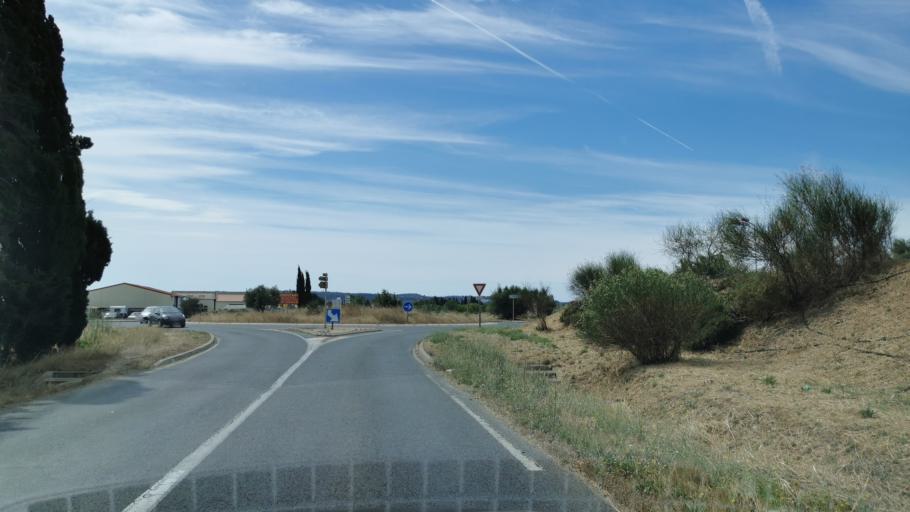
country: FR
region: Languedoc-Roussillon
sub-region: Departement de l'Aude
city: Saint-Marcel-sur-Aude
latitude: 43.2566
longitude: 2.9100
